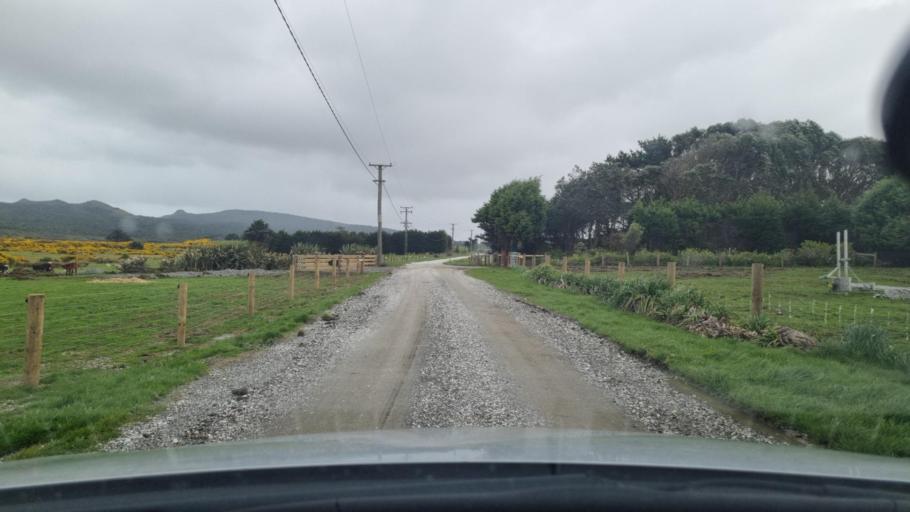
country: NZ
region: Southland
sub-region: Invercargill City
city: Bluff
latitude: -46.5430
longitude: 168.2949
